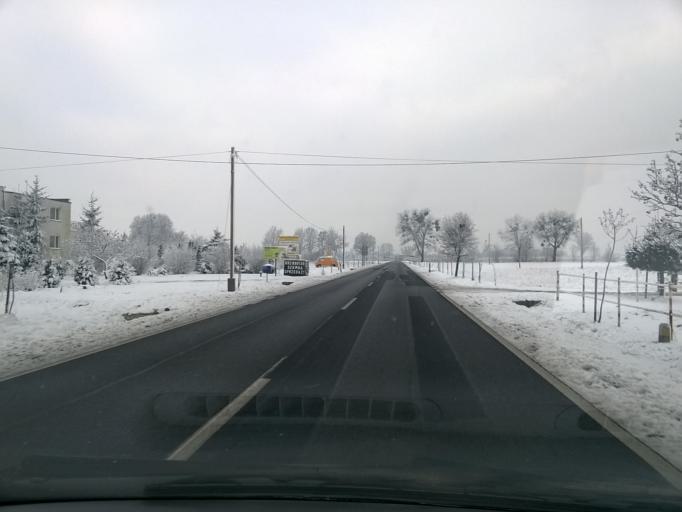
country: PL
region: Kujawsko-Pomorskie
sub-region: Powiat bydgoski
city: Koronowo
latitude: 53.3237
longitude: 17.9156
